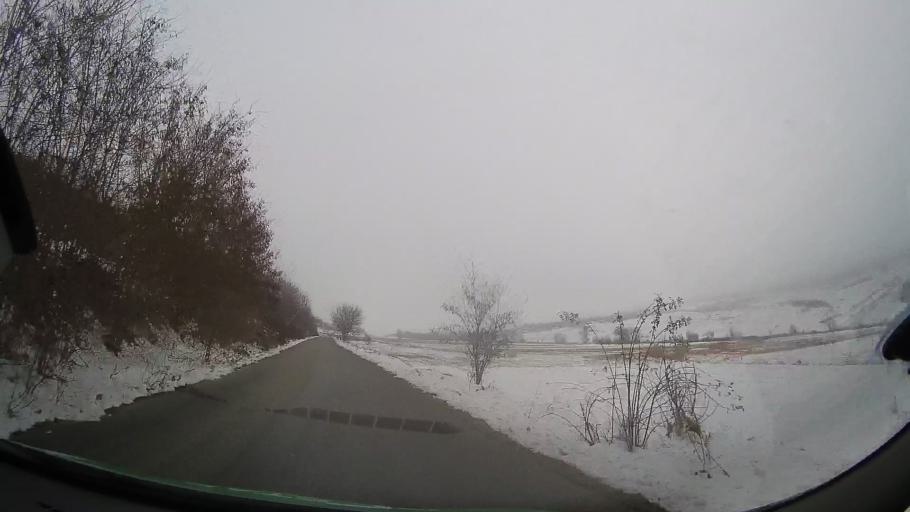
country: RO
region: Bacau
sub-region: Comuna Vultureni
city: Vultureni
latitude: 46.3382
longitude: 27.2905
